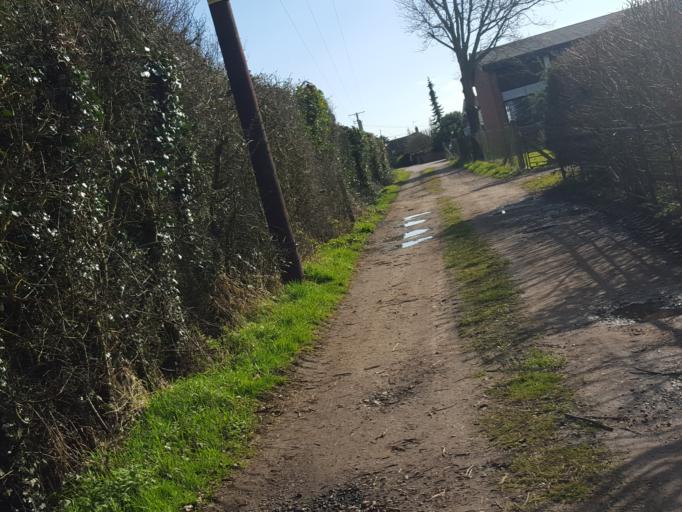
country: GB
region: England
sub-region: Essex
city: Little Clacton
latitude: 51.8607
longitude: 1.1148
